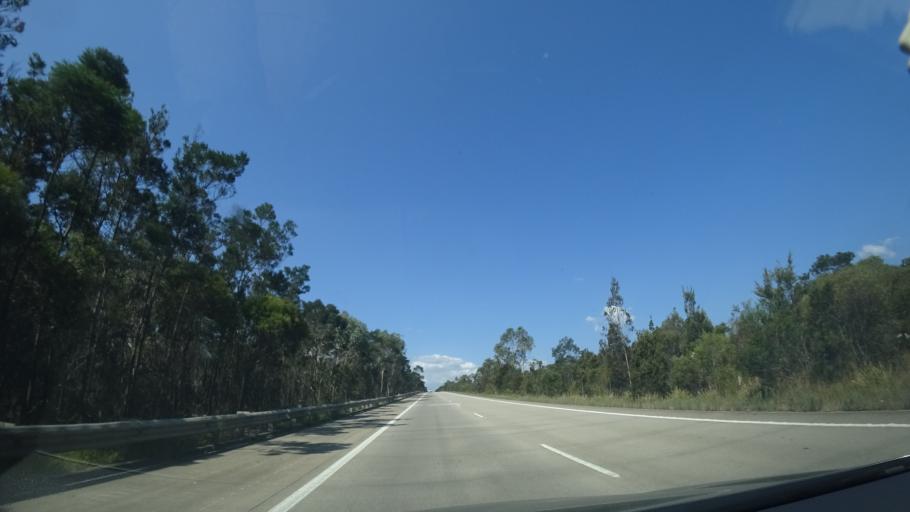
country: AU
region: New South Wales
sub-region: Wingecarribee
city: Colo Vale
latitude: -34.4205
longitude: 150.4813
